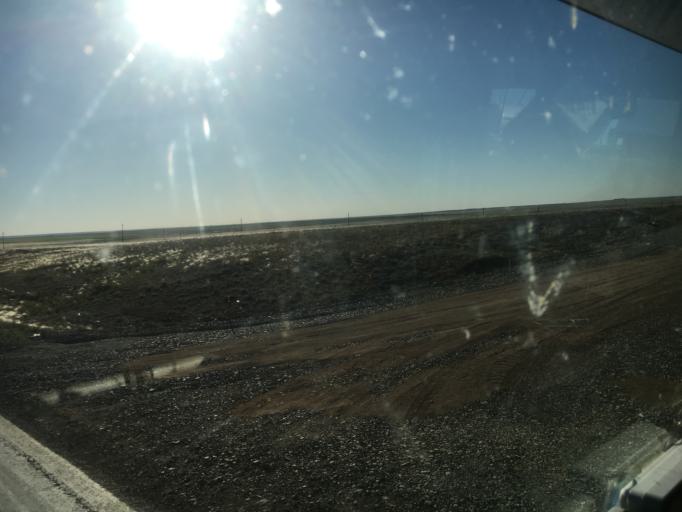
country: KZ
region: Aqtoebe
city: Khromtau
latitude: 50.2571
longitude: 58.3910
